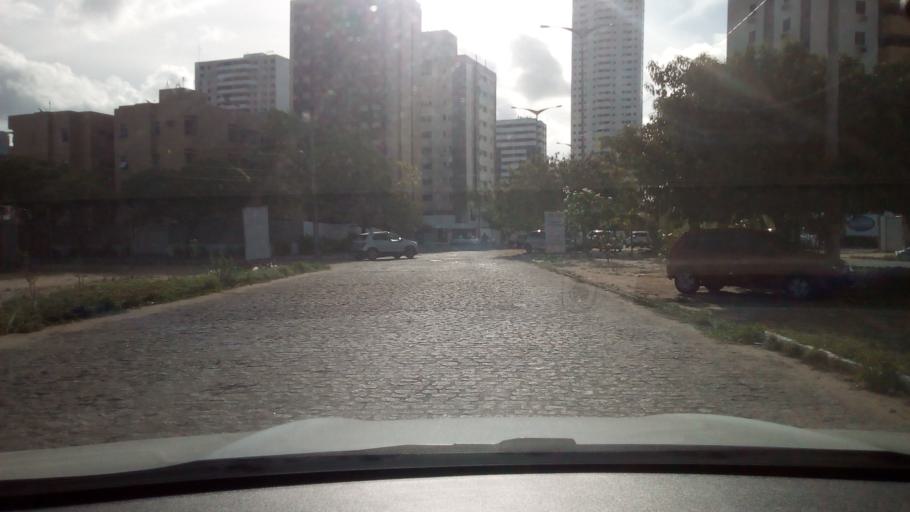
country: BR
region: Paraiba
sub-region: Joao Pessoa
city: Joao Pessoa
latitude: -7.0949
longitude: -34.8412
